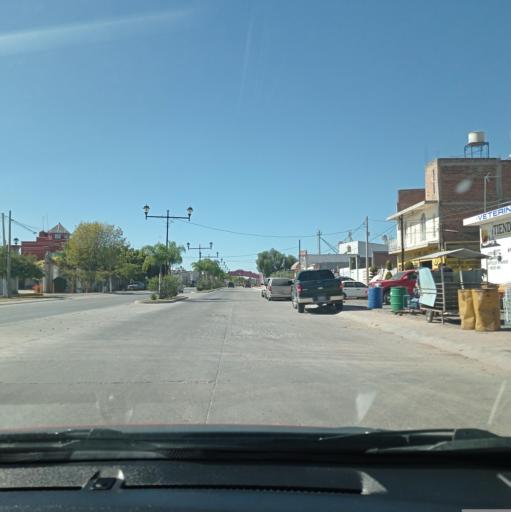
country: MX
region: Jalisco
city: San Julian
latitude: 21.0081
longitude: -102.1640
